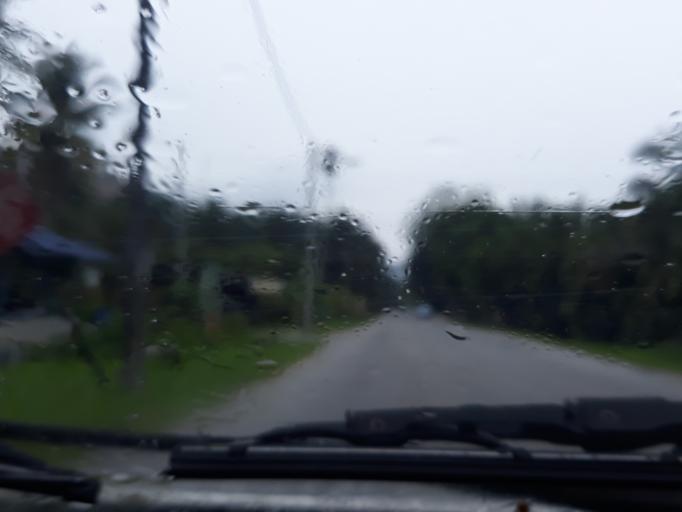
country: MY
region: Kedah
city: Kulim
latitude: 5.2720
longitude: 100.6146
